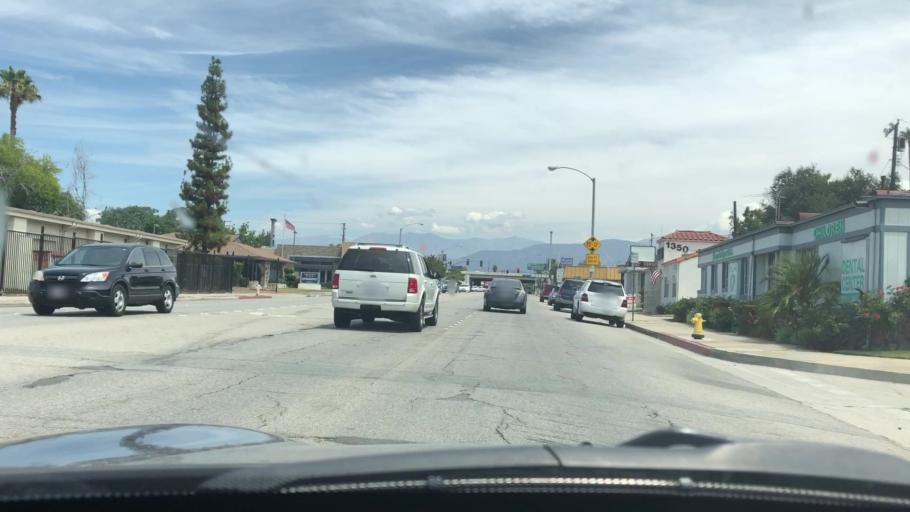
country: US
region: California
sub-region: Los Angeles County
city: Pomona
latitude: 34.0708
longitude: -117.7521
